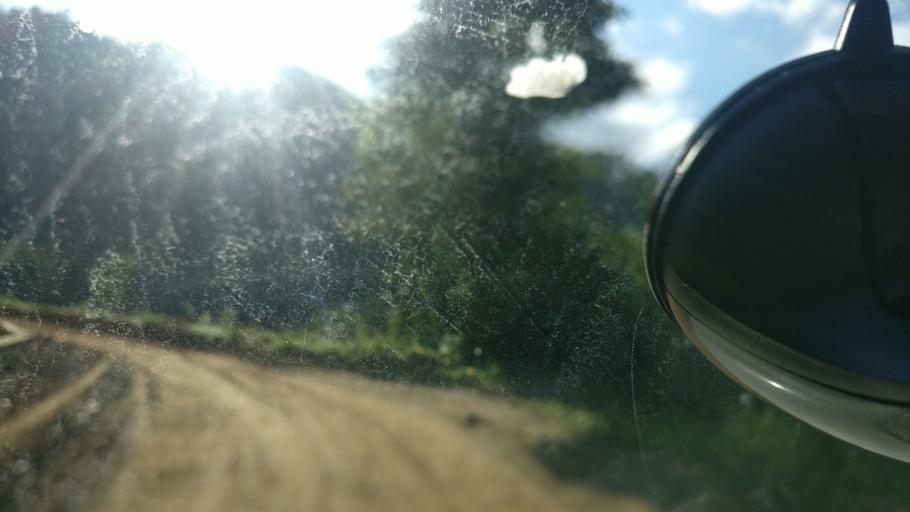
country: NP
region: Western Region
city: Baglung
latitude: 28.1524
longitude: 83.6540
